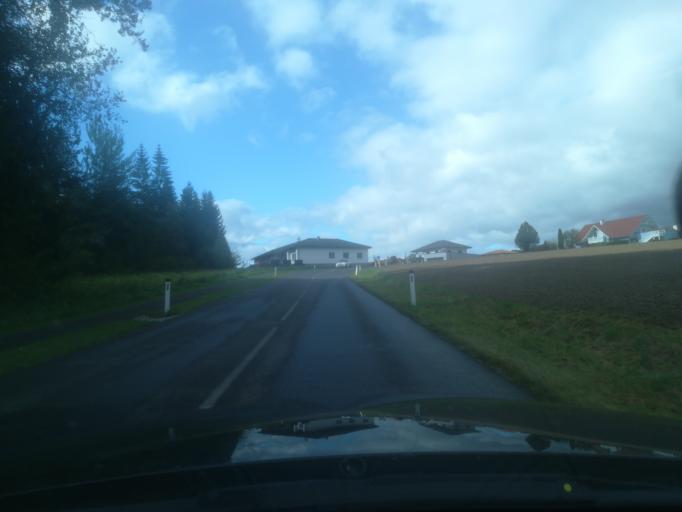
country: AT
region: Upper Austria
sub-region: Politischer Bezirk Urfahr-Umgebung
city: Herzogsdorf
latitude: 48.4315
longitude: 14.1199
